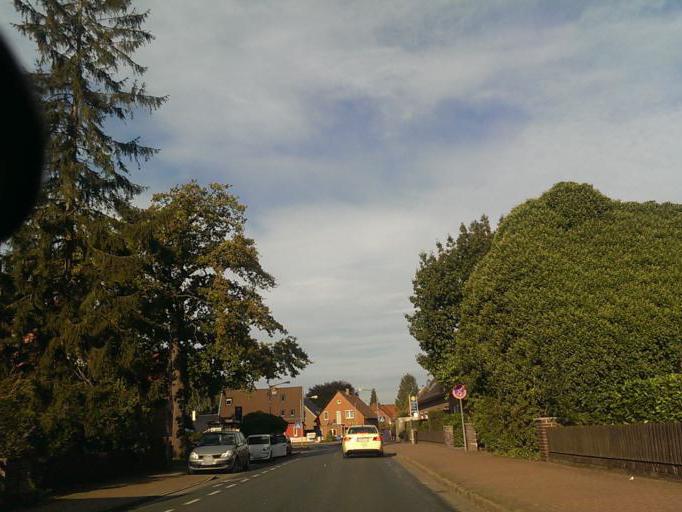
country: DE
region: Lower Saxony
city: Garbsen-Mitte
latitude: 52.4590
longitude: 9.5643
